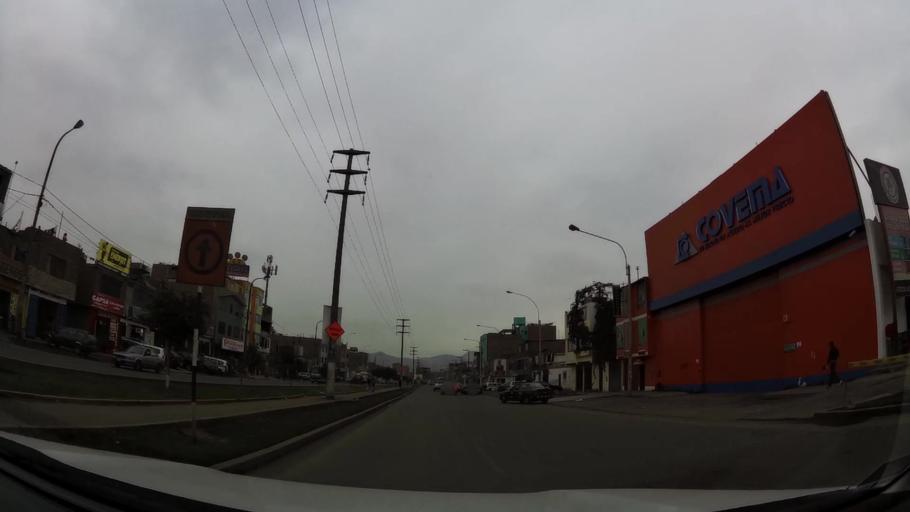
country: PE
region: Lima
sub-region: Lima
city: Vitarte
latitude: -12.0393
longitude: -76.9577
